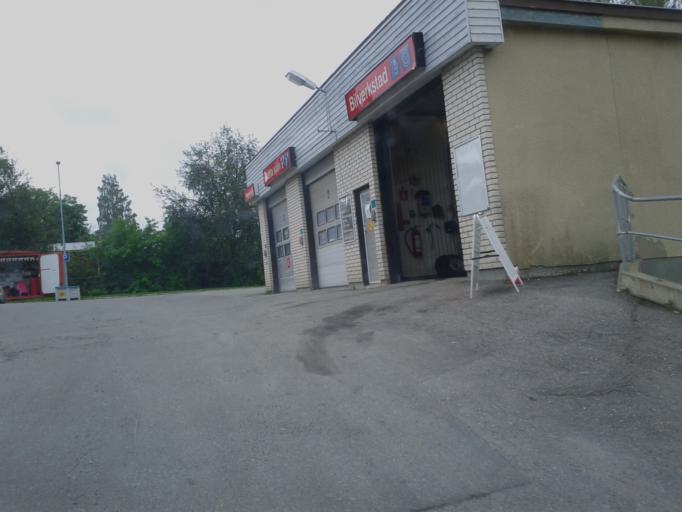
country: SE
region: Vaesterbotten
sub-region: Skelleftea Kommun
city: Boliden
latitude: 64.8694
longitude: 20.3838
